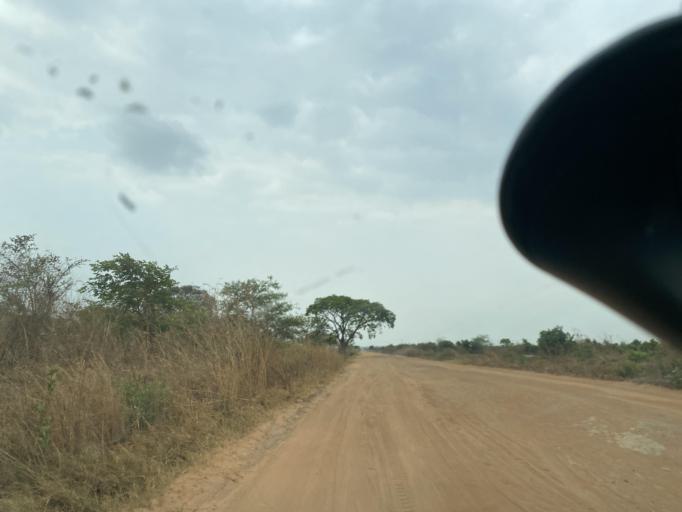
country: ZM
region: Lusaka
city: Lusaka
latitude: -15.2203
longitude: 28.3374
